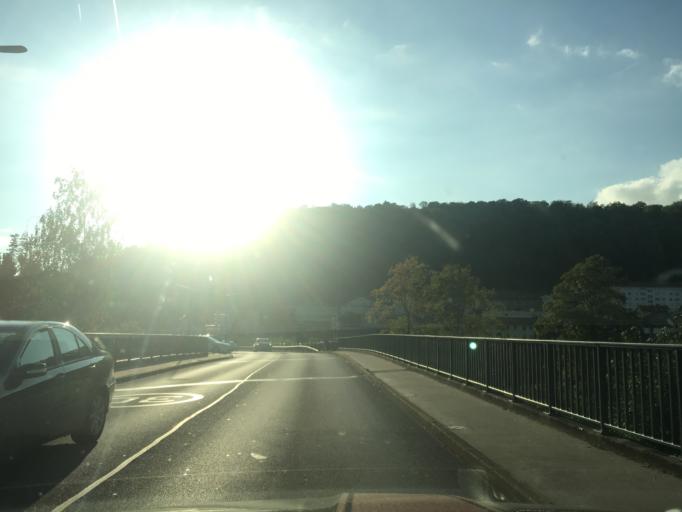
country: FR
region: Lorraine
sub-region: Departement de Meurthe-et-Moselle
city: Longlaville
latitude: 49.5235
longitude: 5.7972
